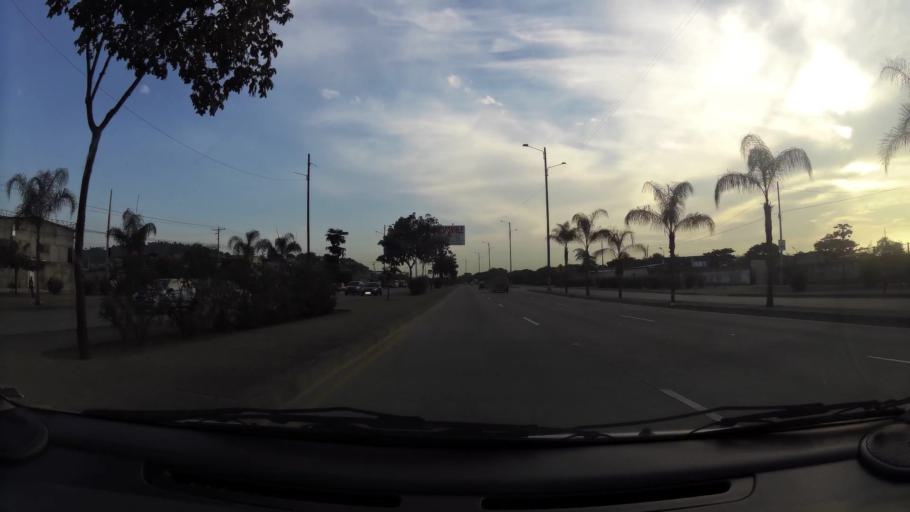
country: EC
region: Guayas
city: Eloy Alfaro
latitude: -2.0818
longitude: -79.8965
